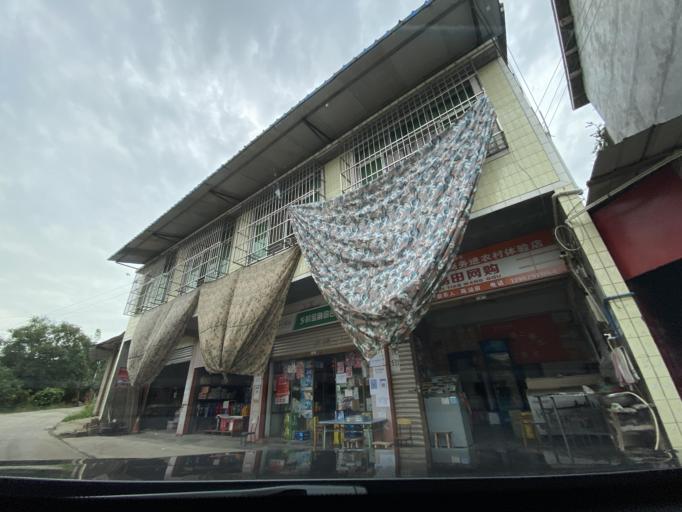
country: CN
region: Sichuan
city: Jiancheng
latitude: 30.3851
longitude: 104.4791
